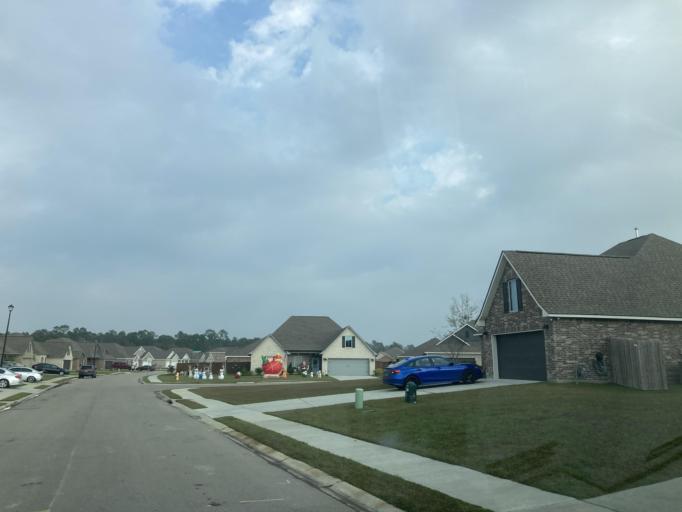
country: US
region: Mississippi
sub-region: Harrison County
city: Long Beach
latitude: 30.3729
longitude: -89.1612
